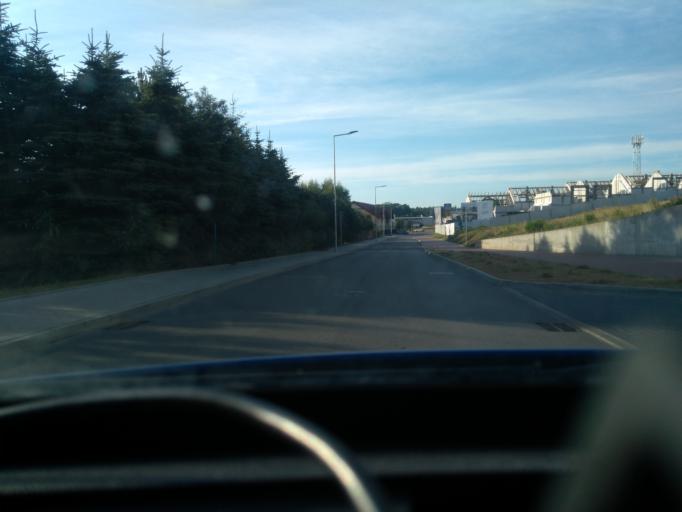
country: PL
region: Pomeranian Voivodeship
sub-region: Powiat kartuski
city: Banino
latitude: 54.3959
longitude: 18.4005
